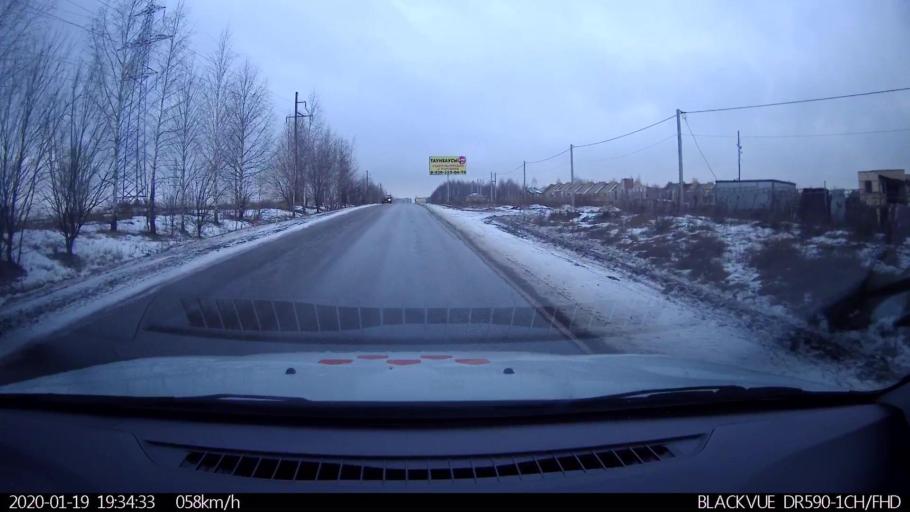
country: RU
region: Nizjnij Novgorod
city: Afonino
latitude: 56.2437
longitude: 44.0781
